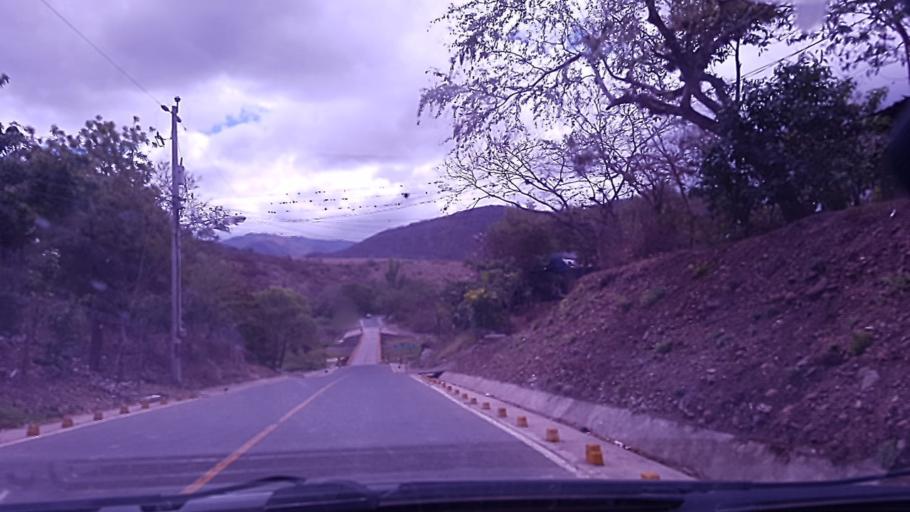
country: NI
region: Esteli
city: Condega
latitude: 13.3766
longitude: -86.3878
